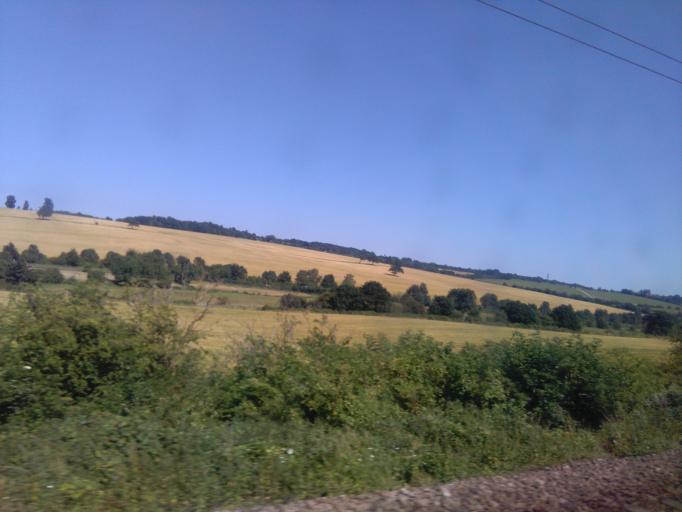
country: GB
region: England
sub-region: Hertfordshire
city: Harpenden
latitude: 51.8353
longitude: -0.3587
